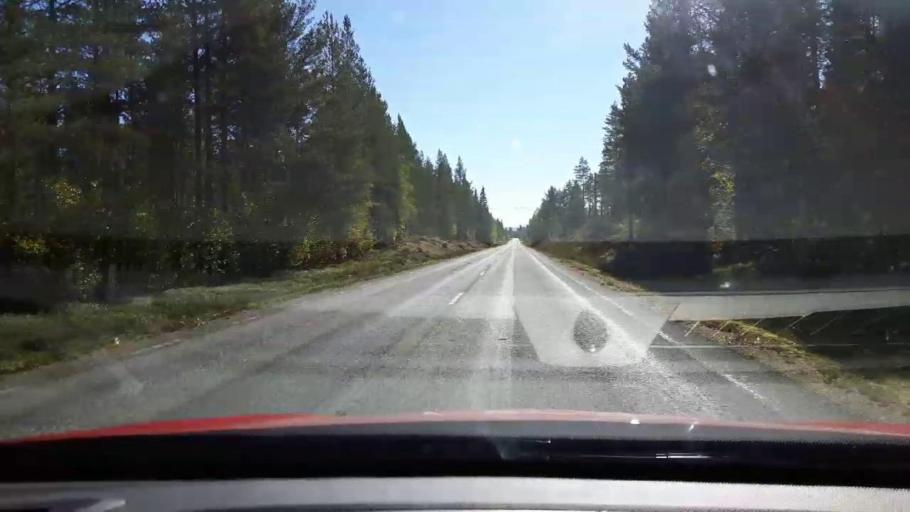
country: SE
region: Jaemtland
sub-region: Harjedalens Kommun
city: Sveg
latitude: 62.3717
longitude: 13.9827
